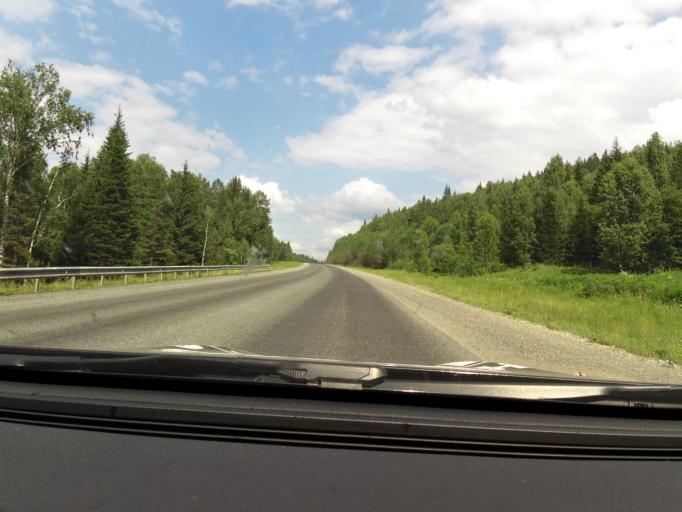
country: RU
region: Sverdlovsk
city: Arti
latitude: 56.7838
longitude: 58.4258
